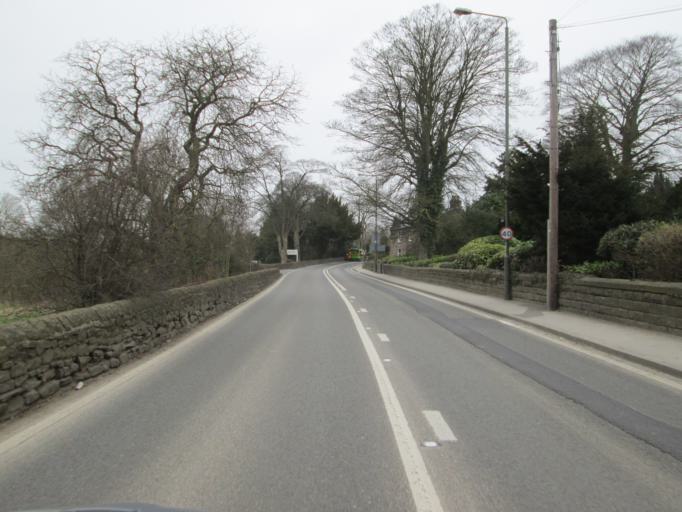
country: GB
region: England
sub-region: Derbyshire
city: Matlock
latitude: 53.1505
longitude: -1.5757
